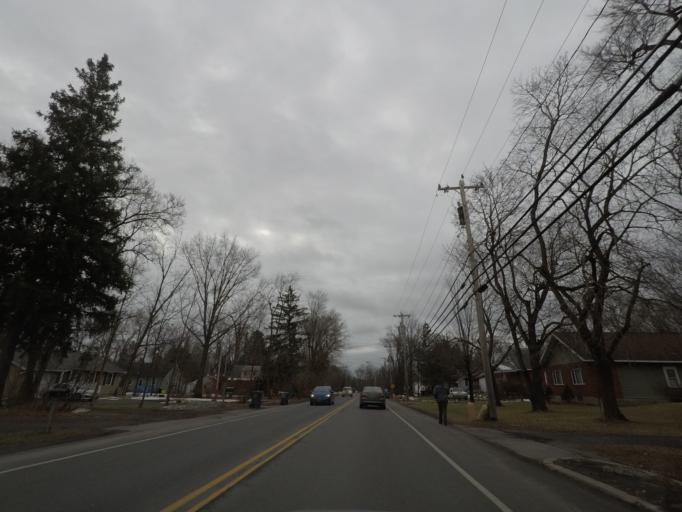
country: US
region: New York
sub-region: Schenectady County
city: East Glenville
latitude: 42.8801
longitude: -73.9288
